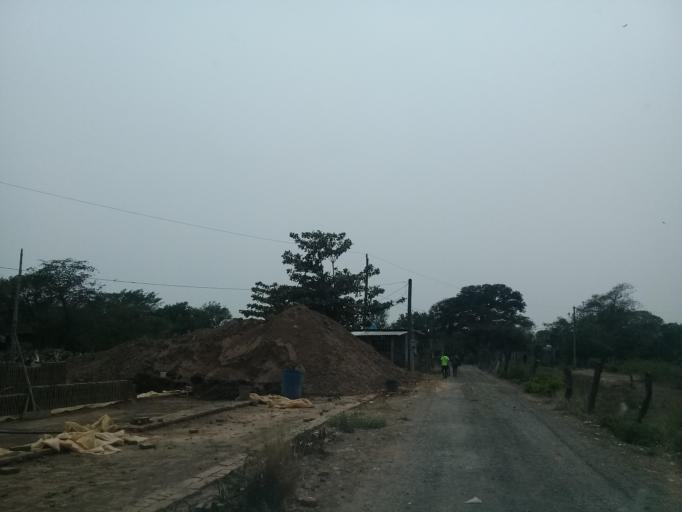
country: MX
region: Veracruz
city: Paso del Toro
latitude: 18.9819
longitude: -96.1744
